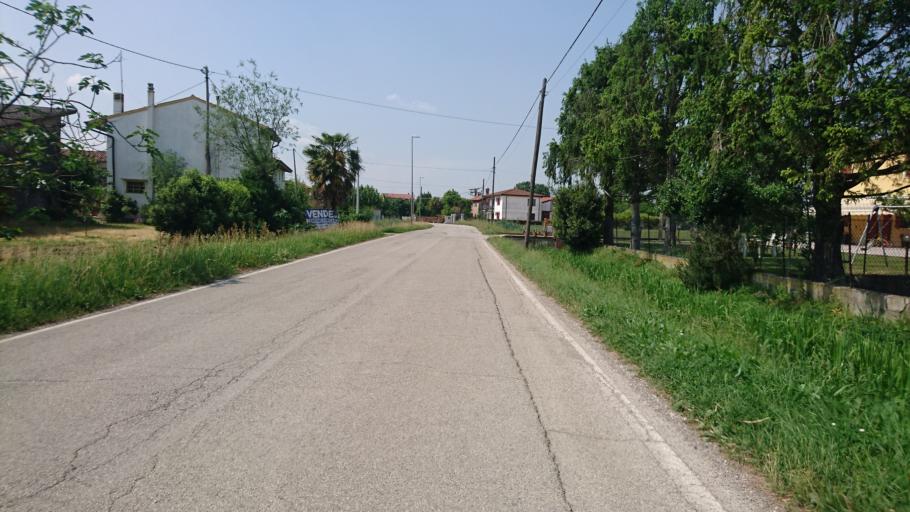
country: IT
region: Veneto
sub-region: Provincia di Venezia
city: Campagna Lupia
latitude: 45.3700
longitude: 12.1105
